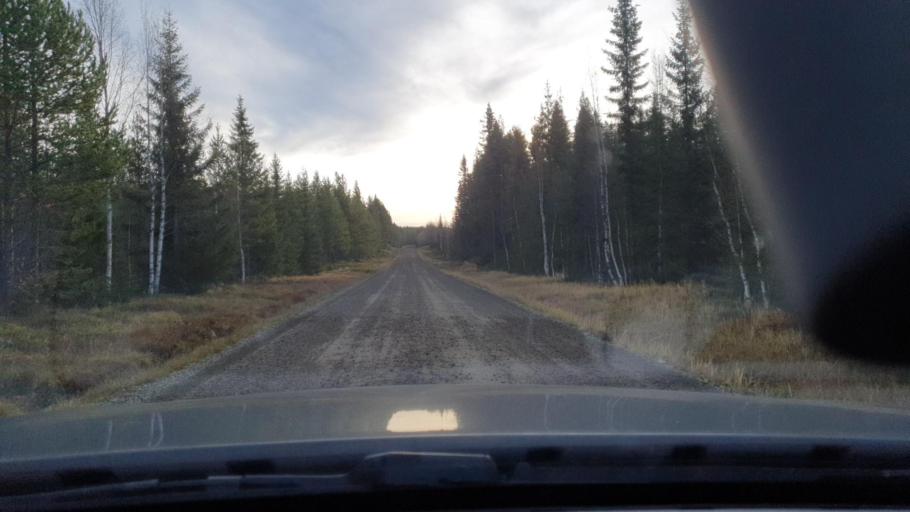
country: SE
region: Jaemtland
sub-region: Stroemsunds Kommun
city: Stroemsund
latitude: 63.5391
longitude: 15.5924
